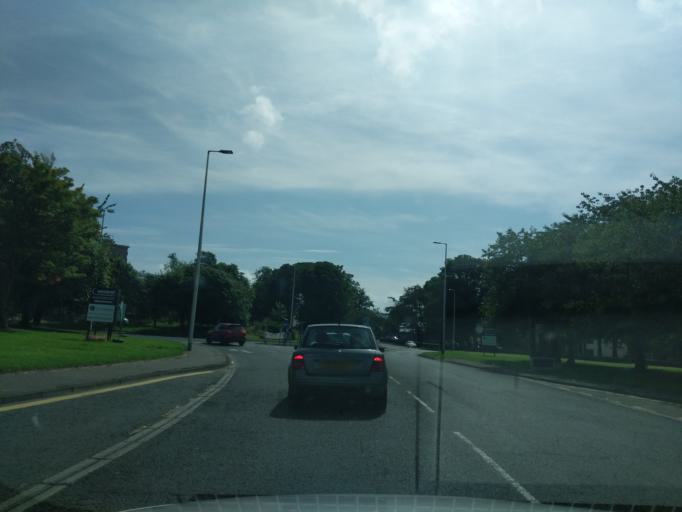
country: GB
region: Scotland
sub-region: Dundee City
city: Dundee
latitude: 56.4808
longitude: -3.0184
